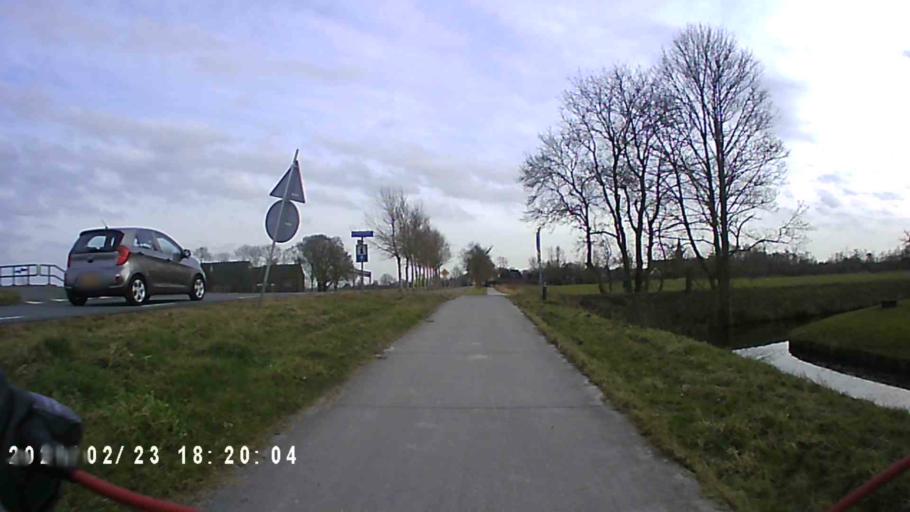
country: NL
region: Groningen
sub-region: Gemeente Bedum
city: Bedum
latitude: 53.3704
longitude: 6.6324
